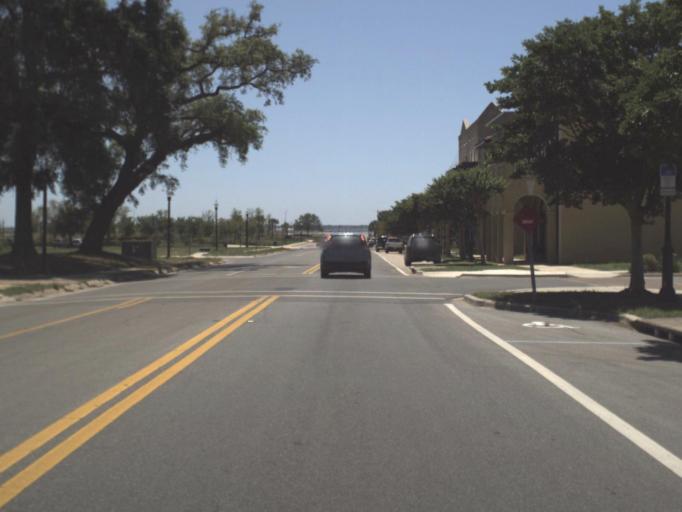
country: US
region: Florida
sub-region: Escambia County
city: Pensacola
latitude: 30.4145
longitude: -87.2052
